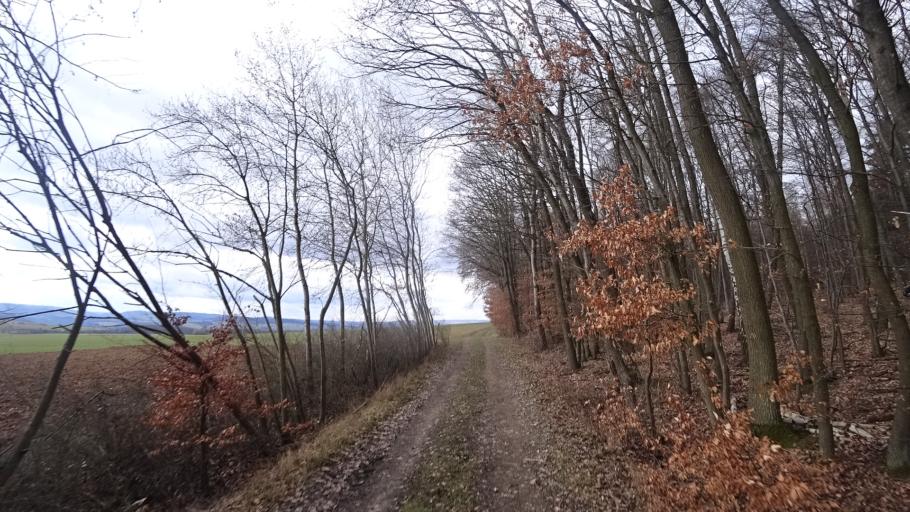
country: DE
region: Rheinland-Pfalz
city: Reitzenhain
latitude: 50.1429
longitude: 7.7780
